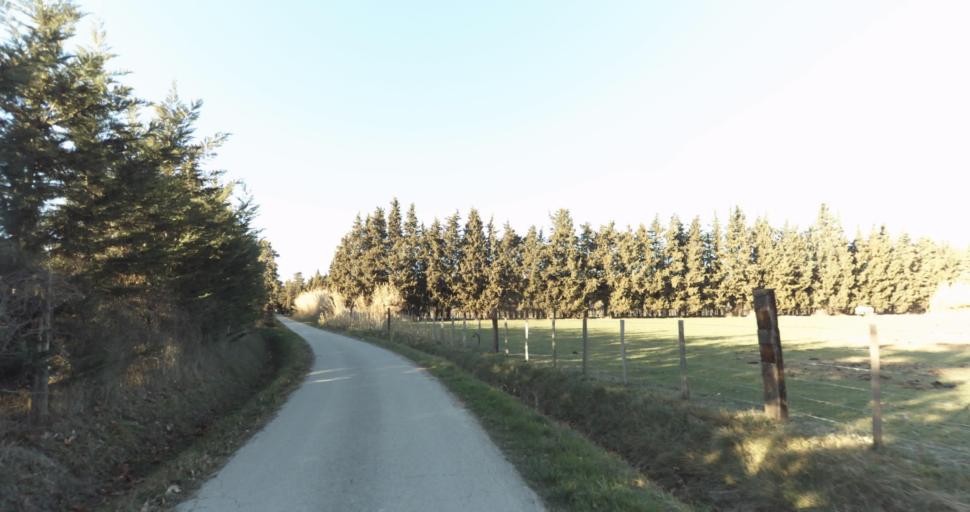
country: FR
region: Provence-Alpes-Cote d'Azur
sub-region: Departement des Bouches-du-Rhone
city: Barbentane
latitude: 43.9150
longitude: 4.7477
